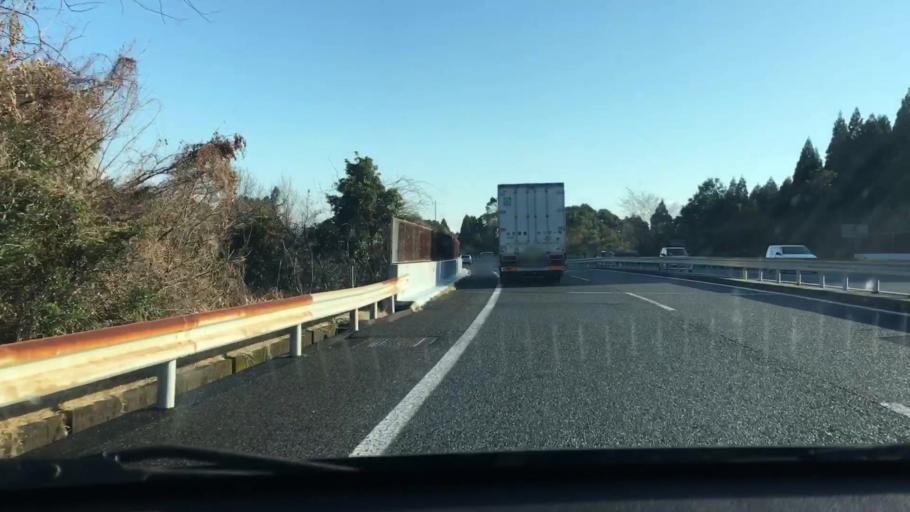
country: JP
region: Kagoshima
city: Kajiki
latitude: 31.8234
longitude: 130.6941
